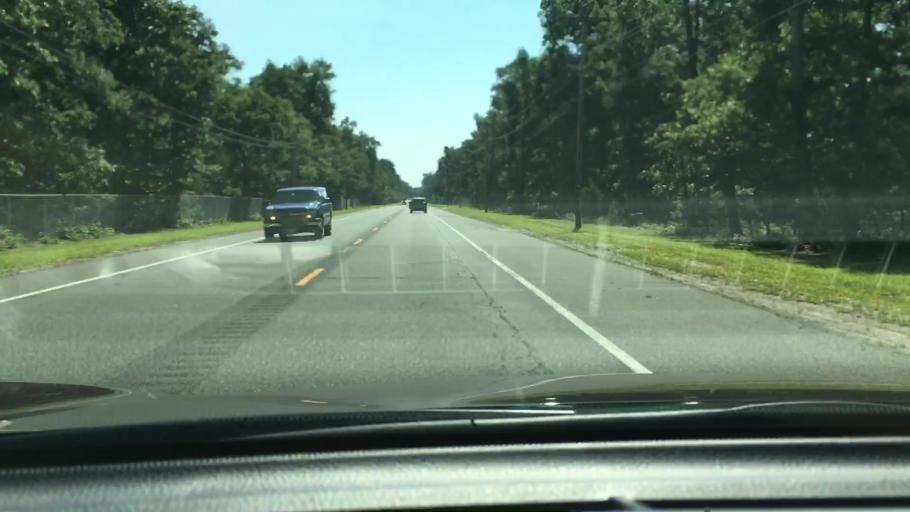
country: US
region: New Jersey
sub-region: Cumberland County
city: Laurel Lake
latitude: 39.3781
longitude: -74.9608
